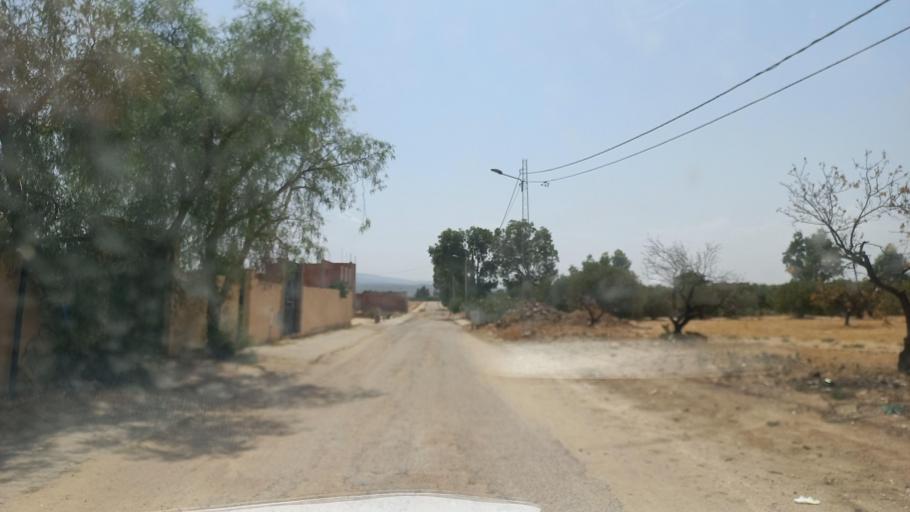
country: TN
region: Al Qasrayn
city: Kasserine
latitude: 35.2501
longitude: 9.0256
